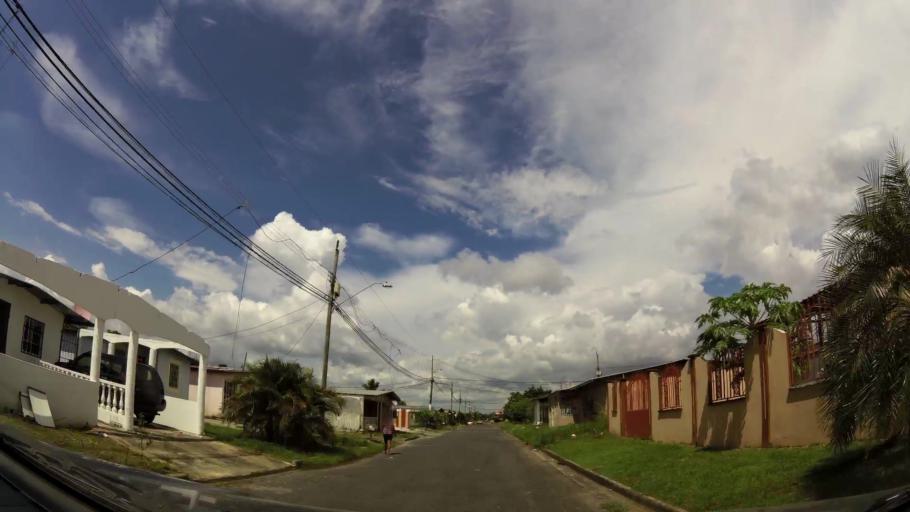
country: PA
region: Panama
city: Nuevo Arraijan
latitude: 8.9039
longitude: -79.7131
